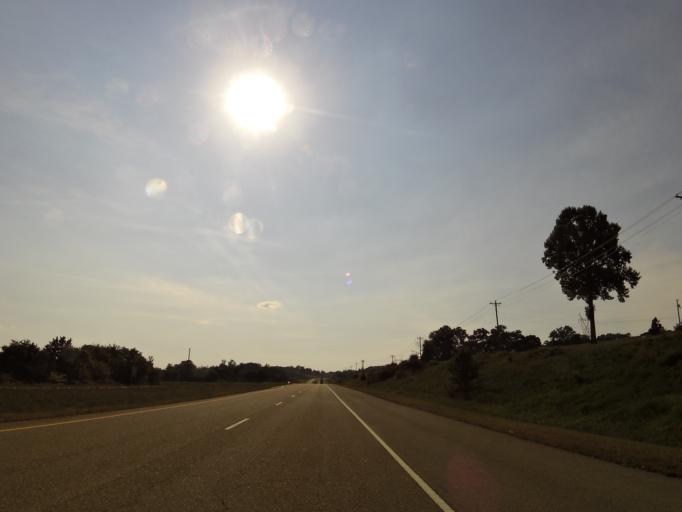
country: US
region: Tennessee
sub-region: Loudon County
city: Greenback
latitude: 35.7372
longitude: -84.1837
